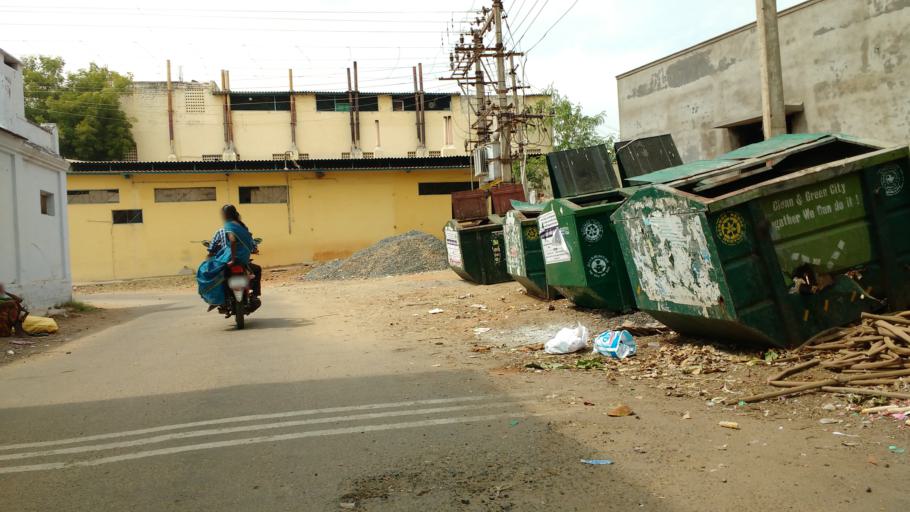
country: IN
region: Tamil Nadu
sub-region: Erode
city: Gobichettipalayam
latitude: 11.4579
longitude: 77.4328
